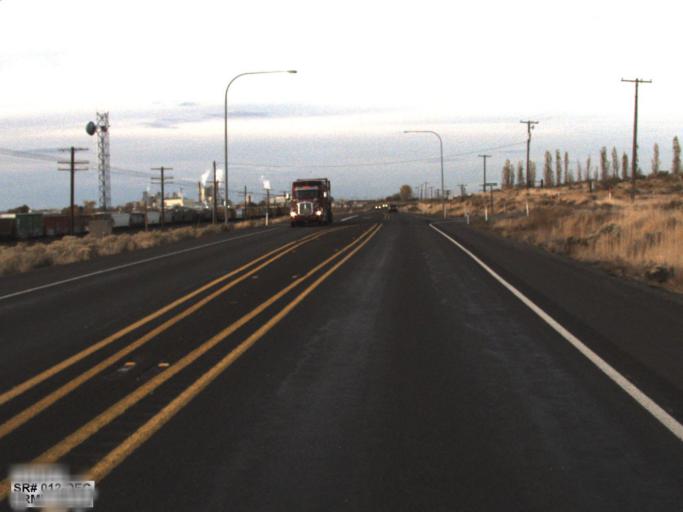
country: US
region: Washington
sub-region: Benton County
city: Finley
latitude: 46.0859
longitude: -118.9097
